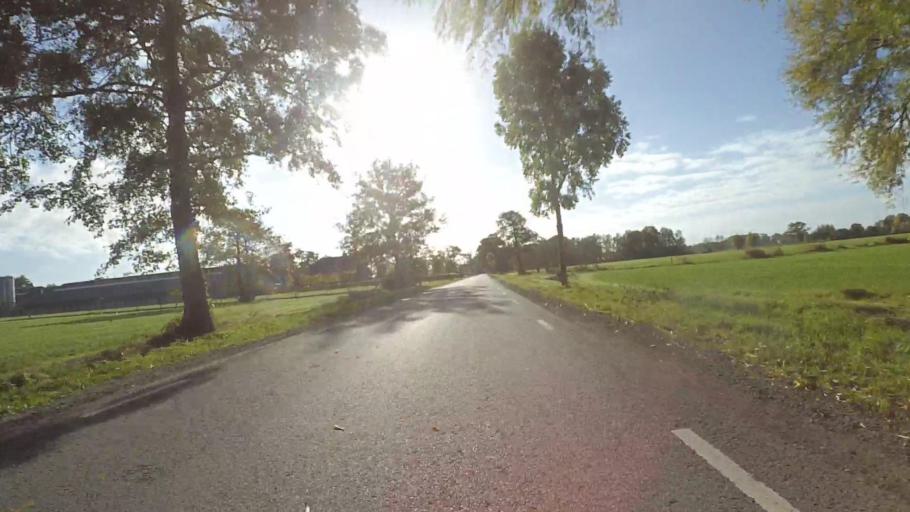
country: NL
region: Gelderland
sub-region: Gemeente Ermelo
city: Horst
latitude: 52.2929
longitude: 5.5653
